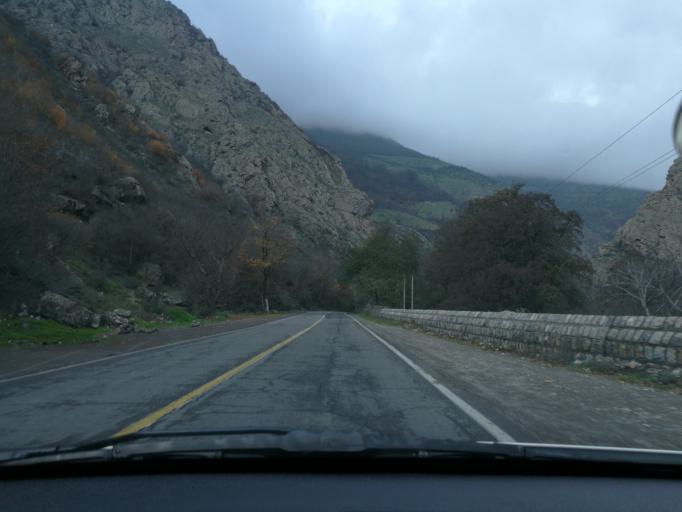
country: IR
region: Mazandaran
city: Chalus
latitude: 36.3605
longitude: 51.2630
